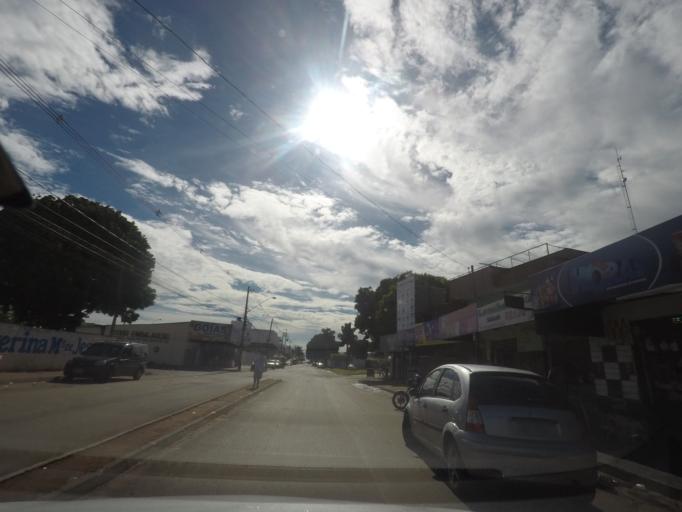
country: BR
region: Goias
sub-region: Aparecida De Goiania
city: Aparecida de Goiania
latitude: -16.8241
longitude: -49.2854
